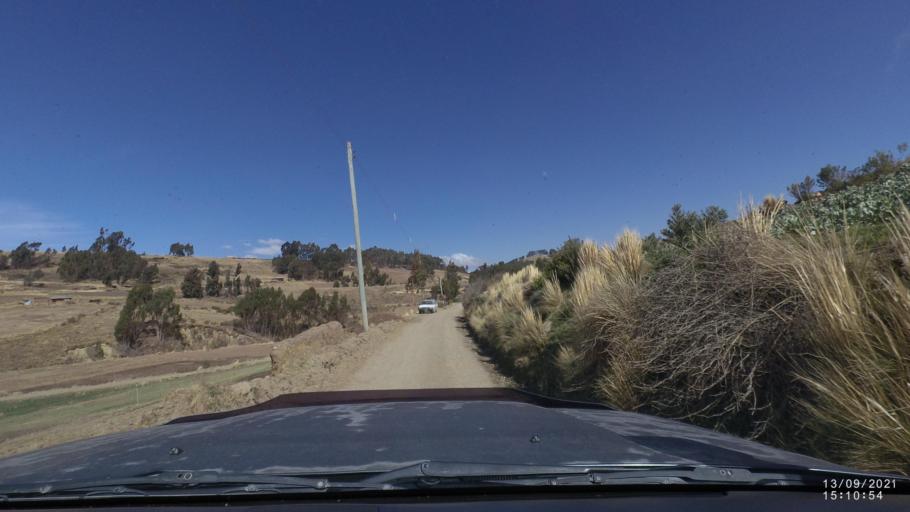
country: BO
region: Cochabamba
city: Colomi
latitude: -17.3571
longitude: -65.8037
